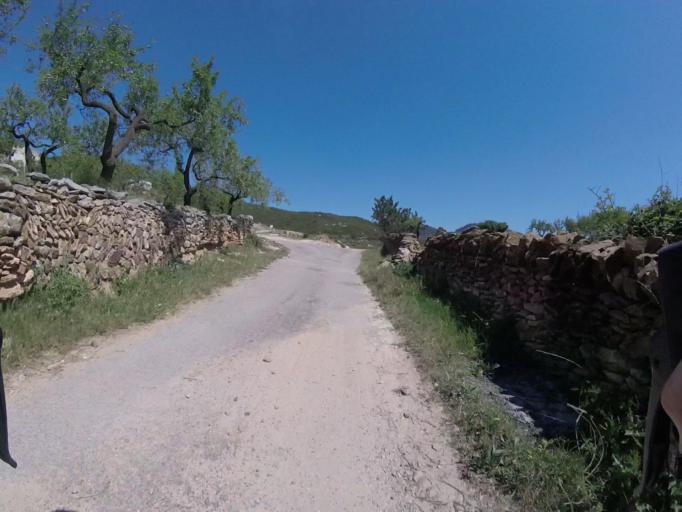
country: ES
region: Valencia
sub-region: Provincia de Castello
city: Sierra-Engarceran
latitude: 40.2491
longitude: -0.0297
